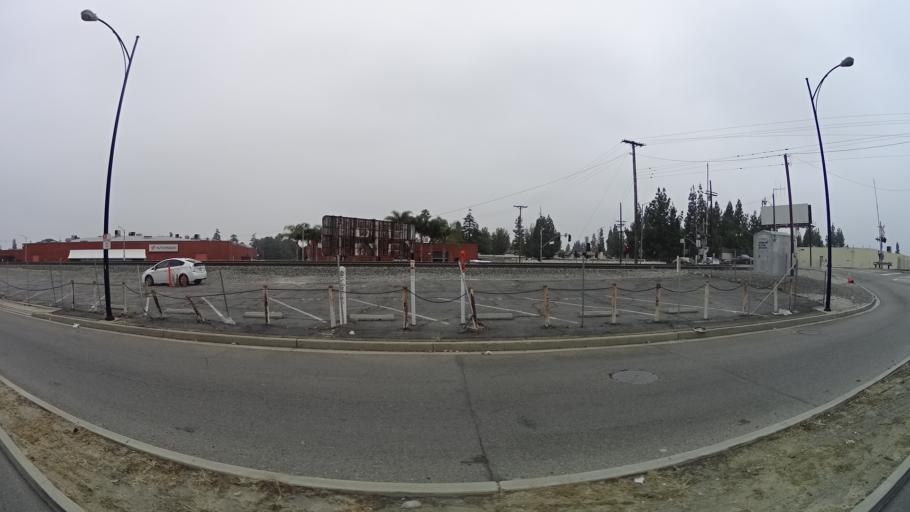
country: US
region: California
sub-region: Los Angeles County
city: North Hollywood
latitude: 34.1945
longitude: -118.3606
